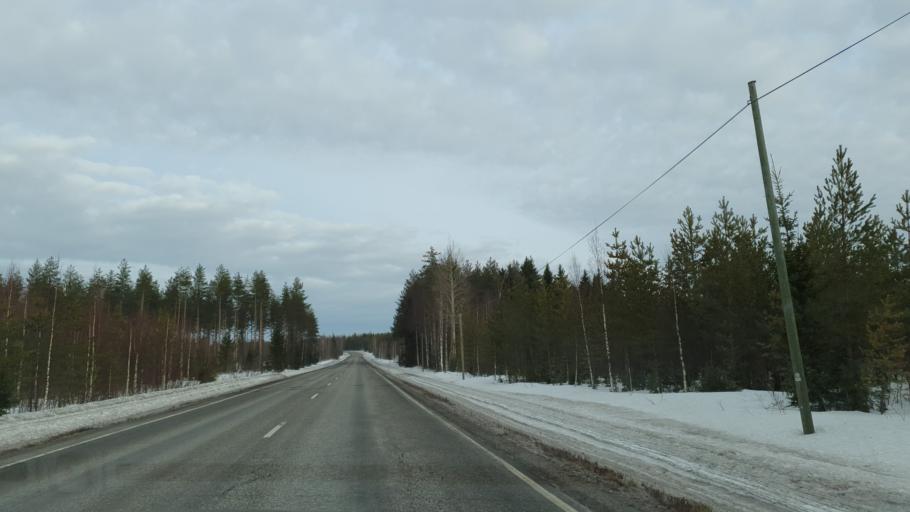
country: FI
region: Kainuu
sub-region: Kajaani
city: Vuokatti
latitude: 64.1937
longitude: 28.1744
